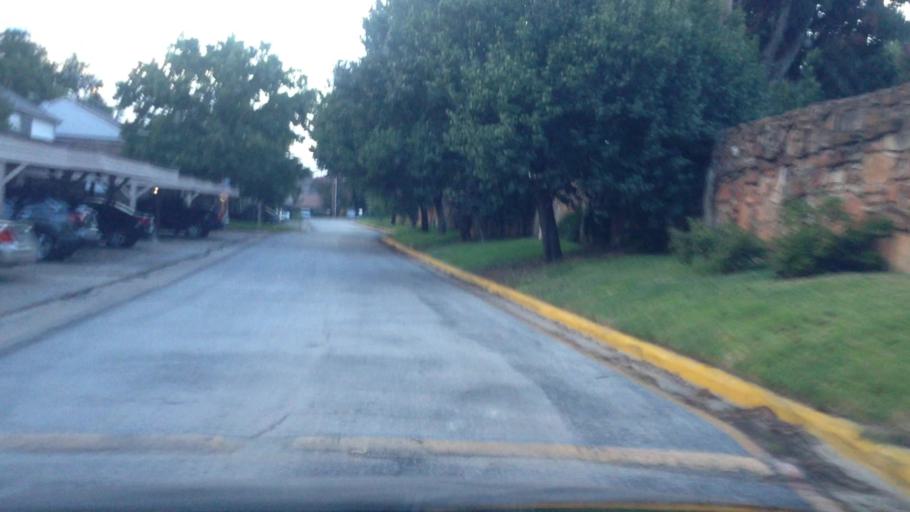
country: US
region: Texas
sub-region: Tarrant County
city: Arlington
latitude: 32.7332
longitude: -97.1326
